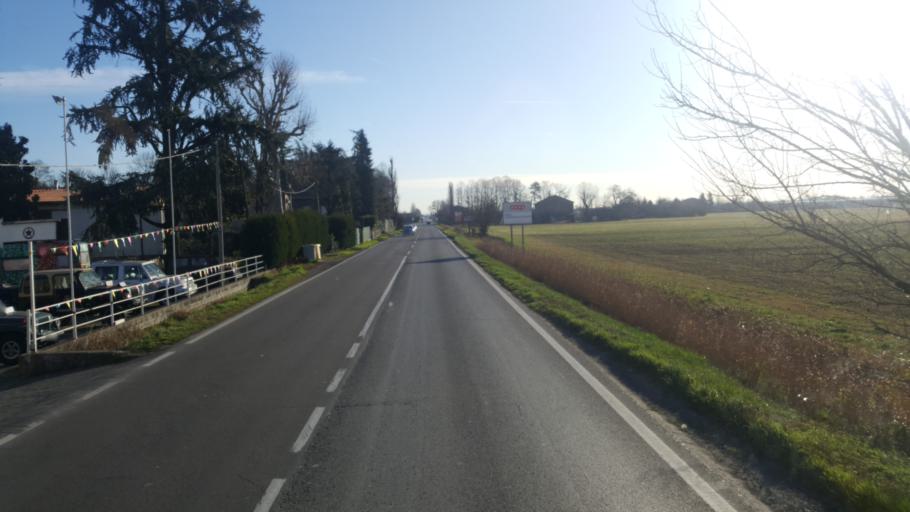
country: IT
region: Emilia-Romagna
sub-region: Provincia di Reggio Emilia
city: Rubiera
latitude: 44.6507
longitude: 10.8138
